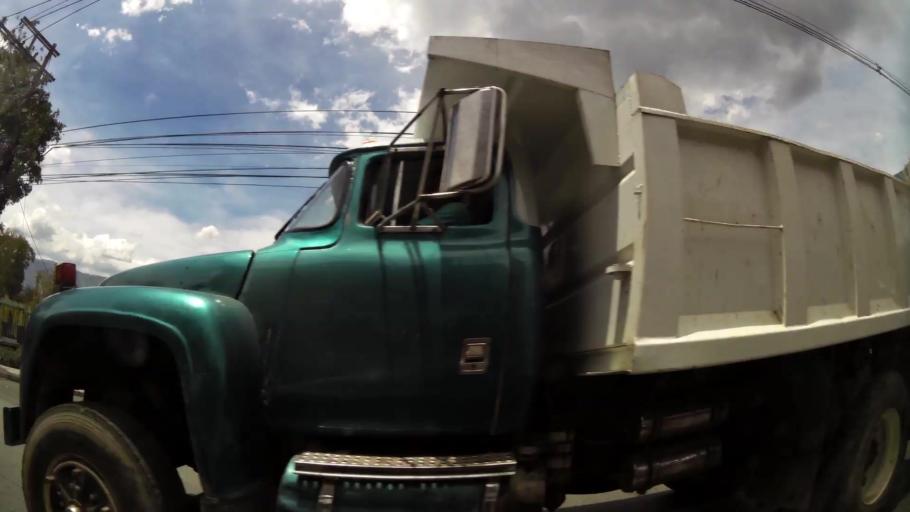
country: CO
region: Antioquia
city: Municipio de Copacabana
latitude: 6.3479
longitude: -75.5084
